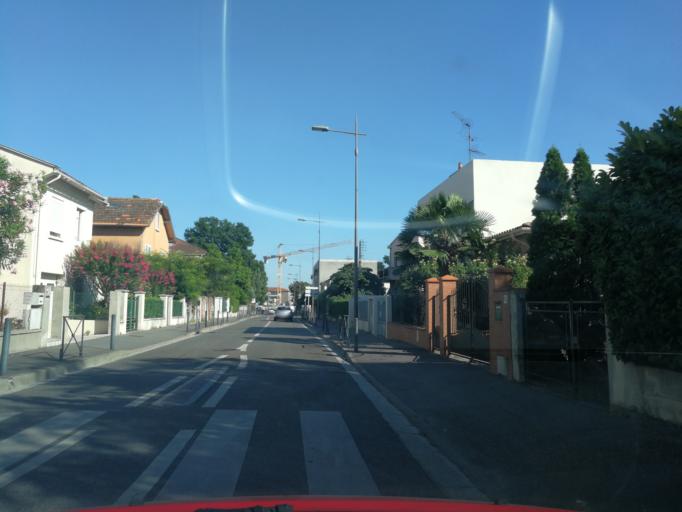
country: FR
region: Midi-Pyrenees
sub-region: Departement de la Haute-Garonne
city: Balma
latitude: 43.6150
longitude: 1.4747
